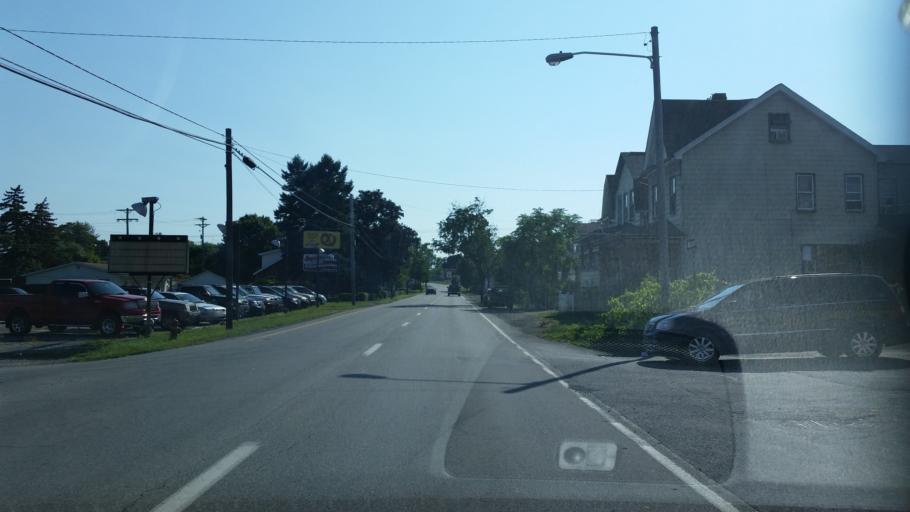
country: US
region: Pennsylvania
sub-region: Blair County
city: Altoona
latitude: 40.5054
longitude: -78.3877
